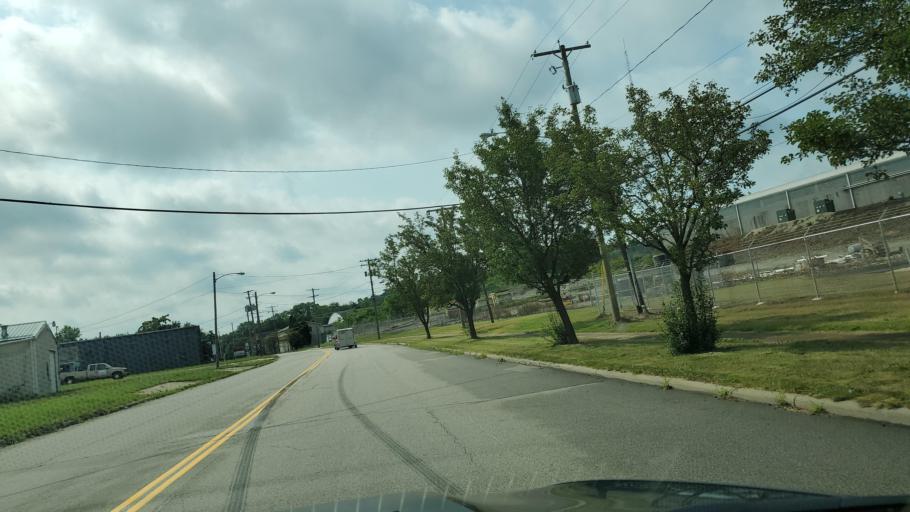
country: US
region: Ohio
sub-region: Mahoning County
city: Youngstown
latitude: 41.0894
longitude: -80.6399
